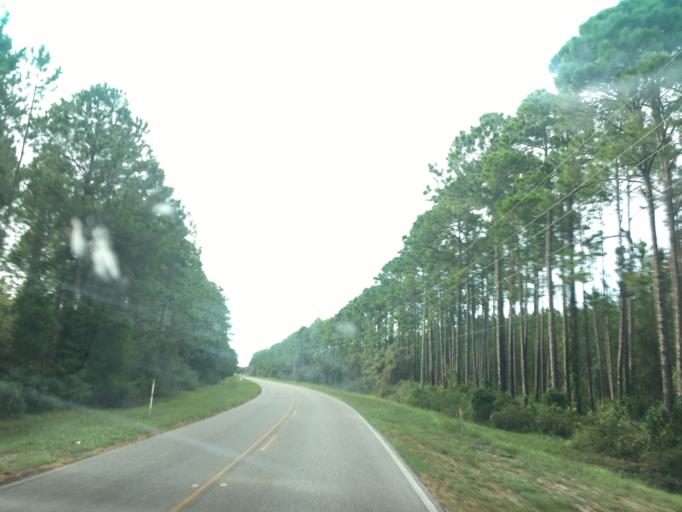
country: US
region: Florida
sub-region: Wakulla County
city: Crawfordville
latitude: 29.9362
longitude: -84.3792
